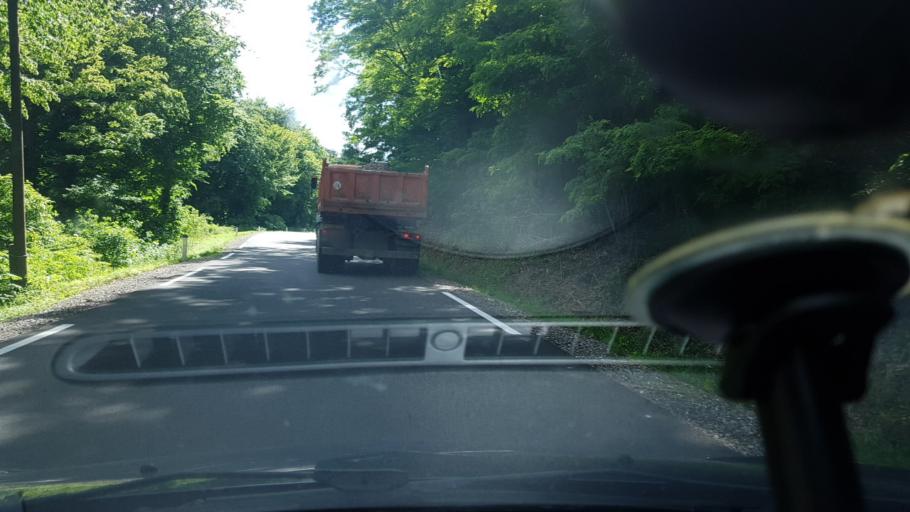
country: SI
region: Zetale
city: Zetale
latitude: 46.2609
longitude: 15.7620
